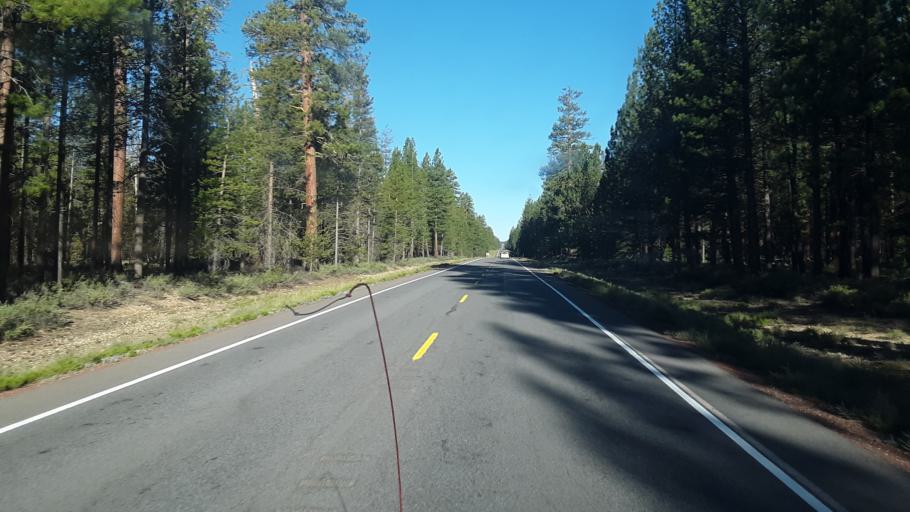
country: US
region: Oregon
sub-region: Deschutes County
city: La Pine
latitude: 43.0857
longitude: -121.9457
